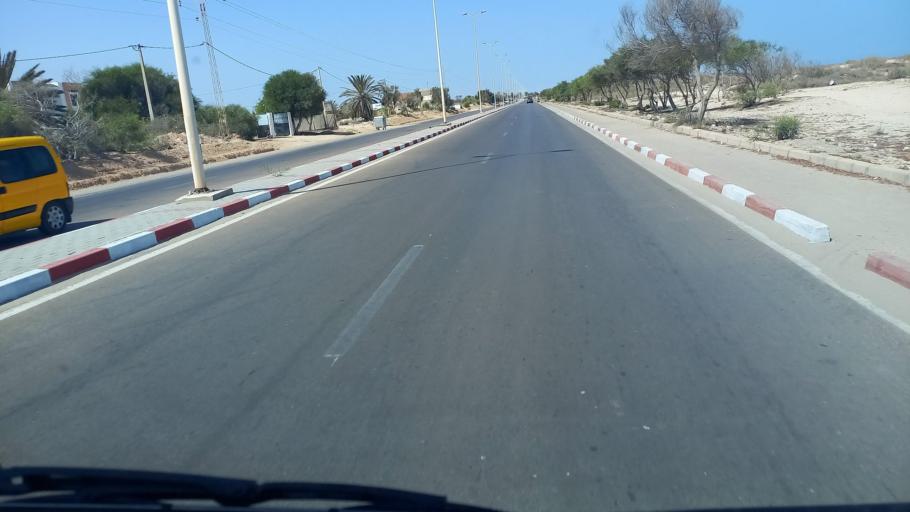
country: TN
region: Madanin
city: Midoun
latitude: 33.8692
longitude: 10.9528
